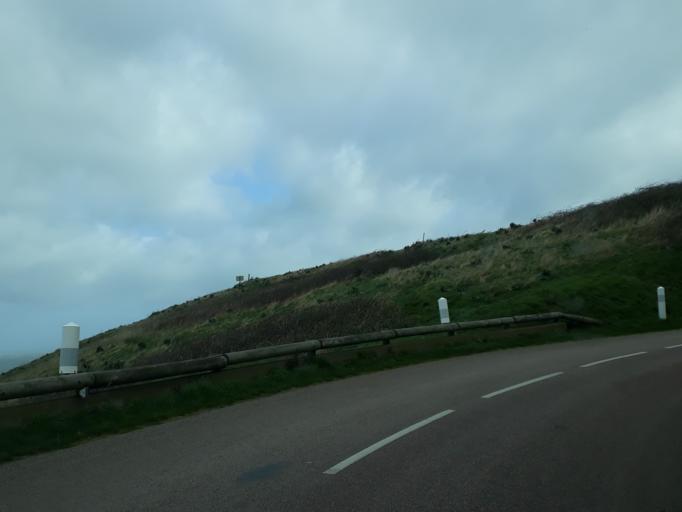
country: FR
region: Haute-Normandie
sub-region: Departement de la Seine-Maritime
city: Yport
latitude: 49.7385
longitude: 0.2933
